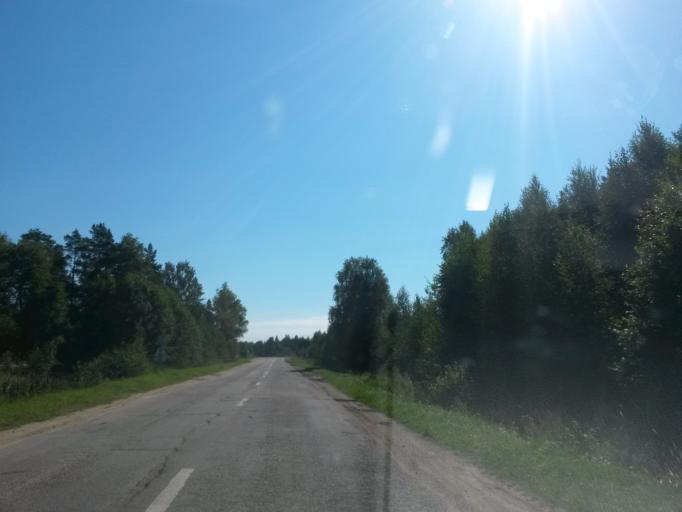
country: RU
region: Jaroslavl
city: Dubki
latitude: 57.2984
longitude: 40.0726
